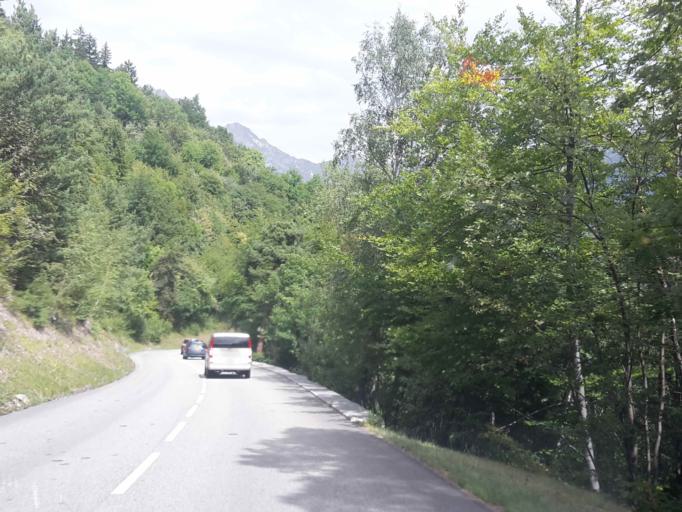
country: FR
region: Rhone-Alpes
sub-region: Departement de la Savoie
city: Saint-Michel-de-Maurienne
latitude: 45.2064
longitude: 6.4535
